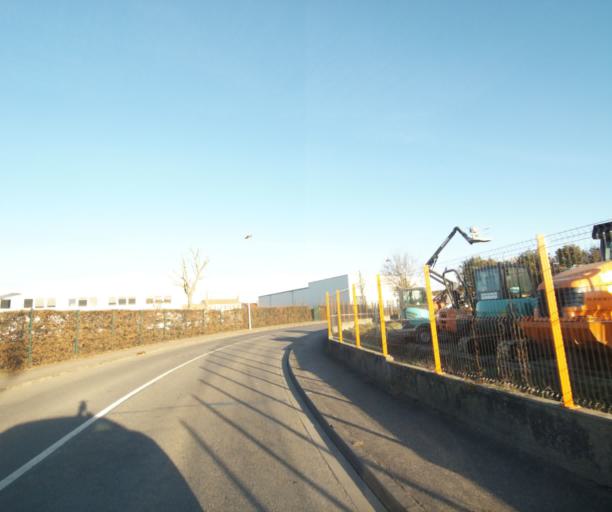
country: FR
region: Lorraine
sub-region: Departement de Meurthe-et-Moselle
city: Pulnoy
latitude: 48.7061
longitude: 6.2539
